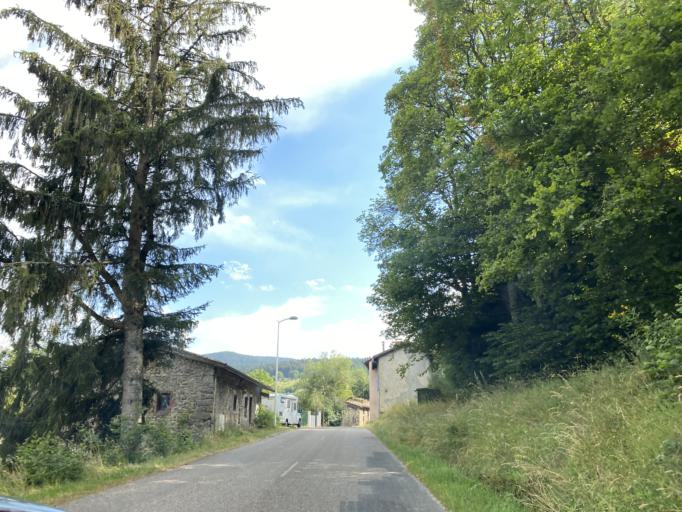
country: FR
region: Rhone-Alpes
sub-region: Departement de la Loire
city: Noiretable
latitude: 45.8019
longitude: 3.7374
